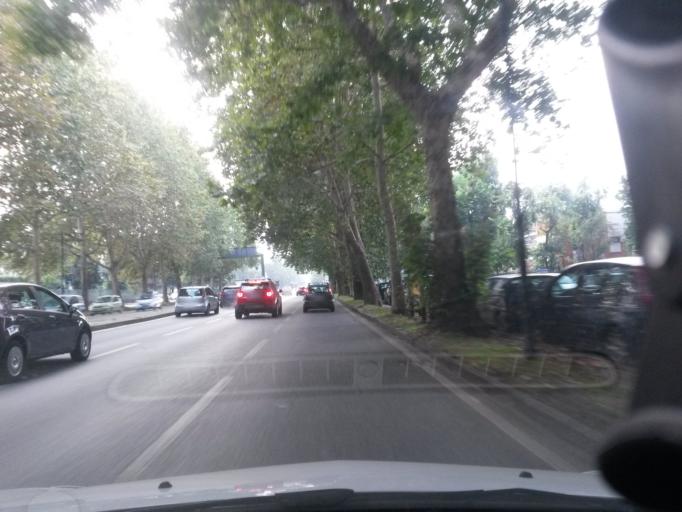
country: IT
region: Piedmont
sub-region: Provincia di Torino
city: Turin
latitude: 45.0866
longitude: 7.6542
